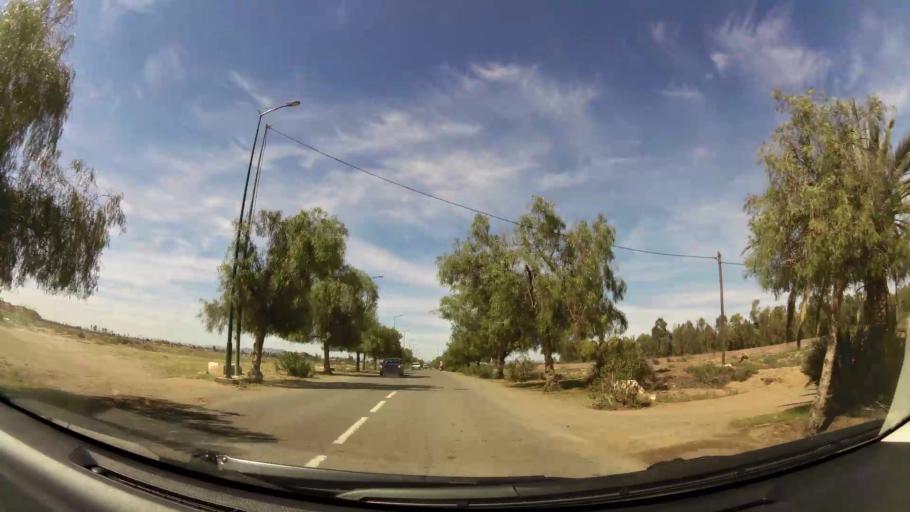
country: MA
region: Marrakech-Tensift-Al Haouz
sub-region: Marrakech
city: Marrakesh
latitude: 31.6100
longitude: -7.9540
